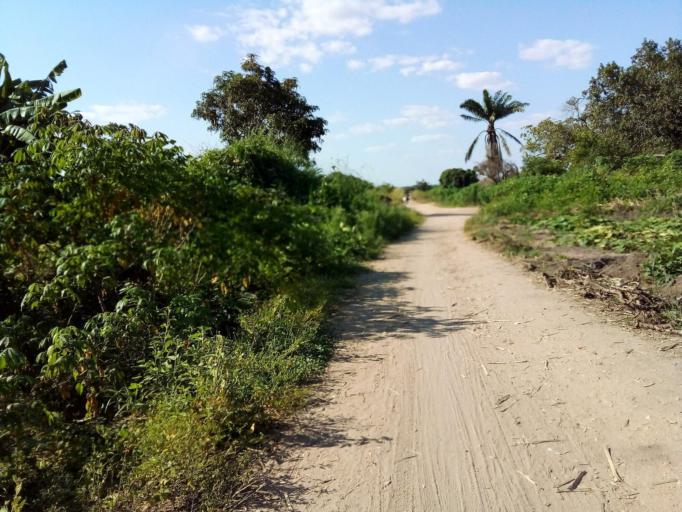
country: MZ
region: Zambezia
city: Quelimane
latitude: -17.5916
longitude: 36.8344
